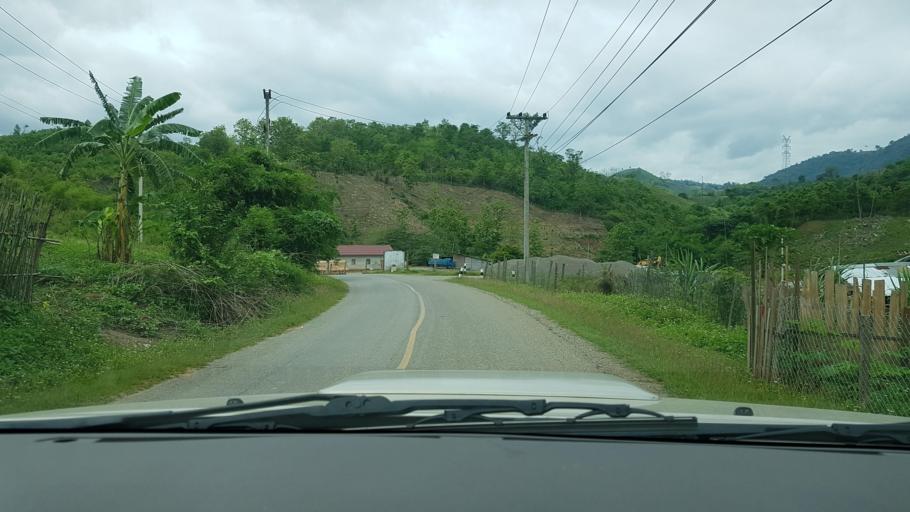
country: TH
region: Nan
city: Chaloem Phra Kiat
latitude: 19.9733
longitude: 101.2674
